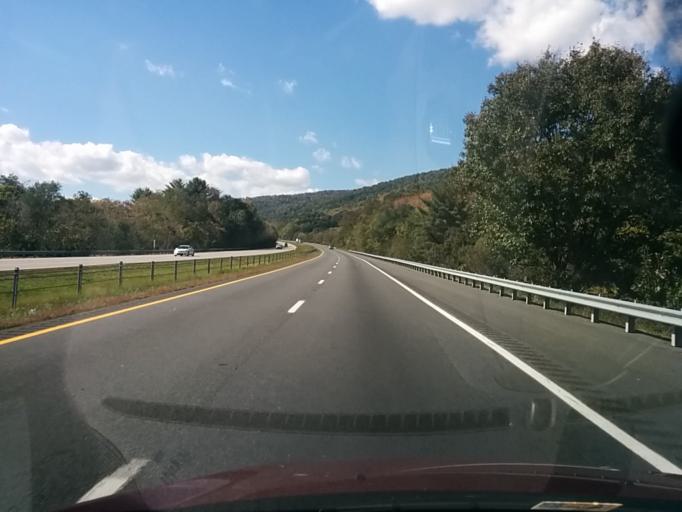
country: US
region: Virginia
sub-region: Albemarle County
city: Crozet
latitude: 38.0468
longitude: -78.7682
